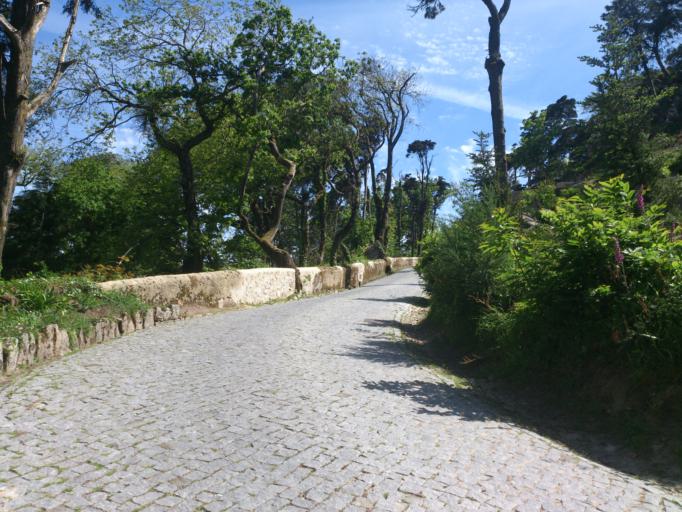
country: PT
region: Lisbon
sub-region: Sintra
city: Sintra
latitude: 38.7888
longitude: -9.3898
